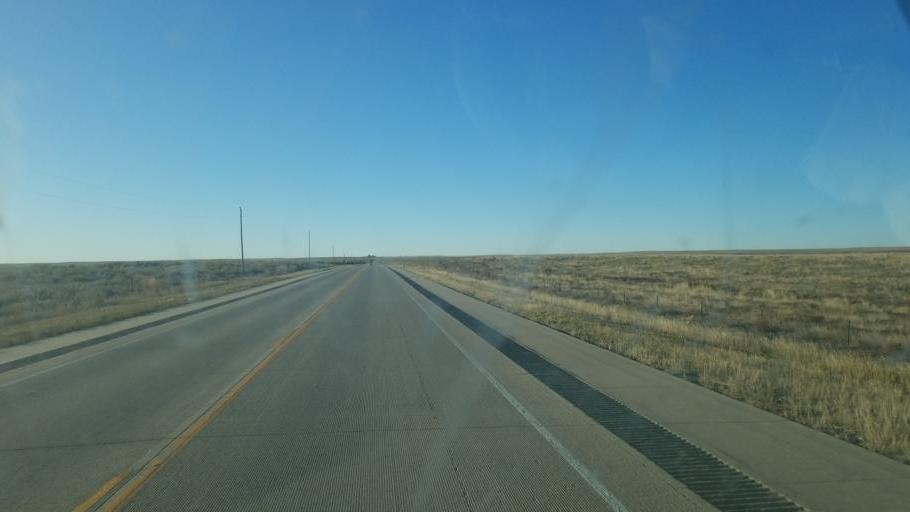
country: US
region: Colorado
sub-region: Kiowa County
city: Eads
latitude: 38.6282
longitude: -102.7860
